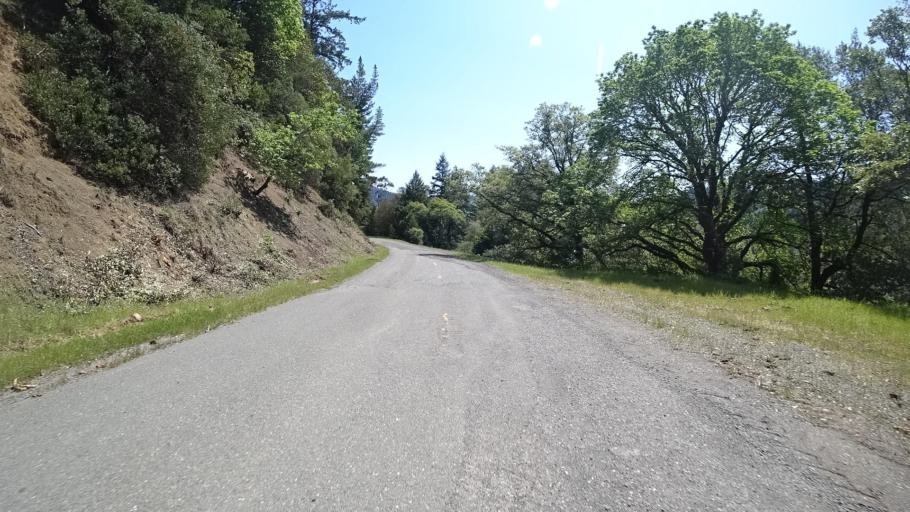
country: US
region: California
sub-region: Humboldt County
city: Redway
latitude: 40.2290
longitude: -123.6457
